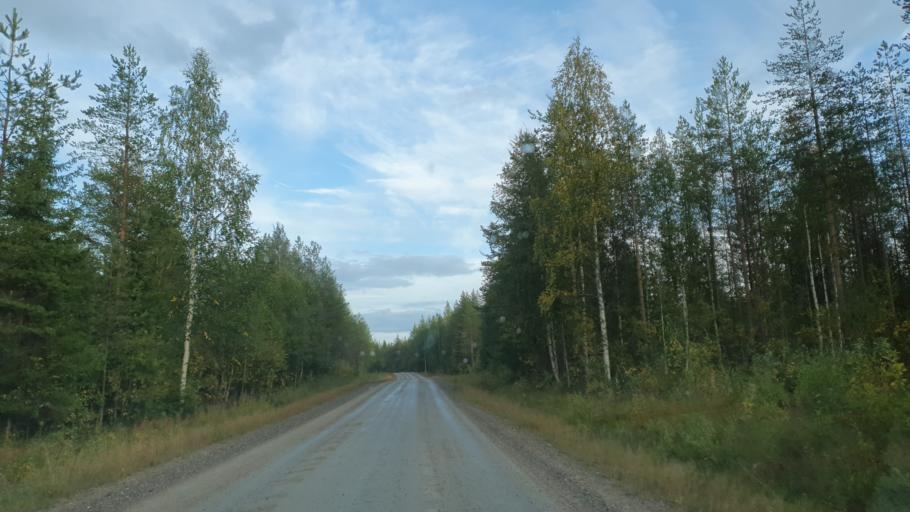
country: FI
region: Kainuu
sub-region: Kehys-Kainuu
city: Kuhmo
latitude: 64.4169
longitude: 29.5032
